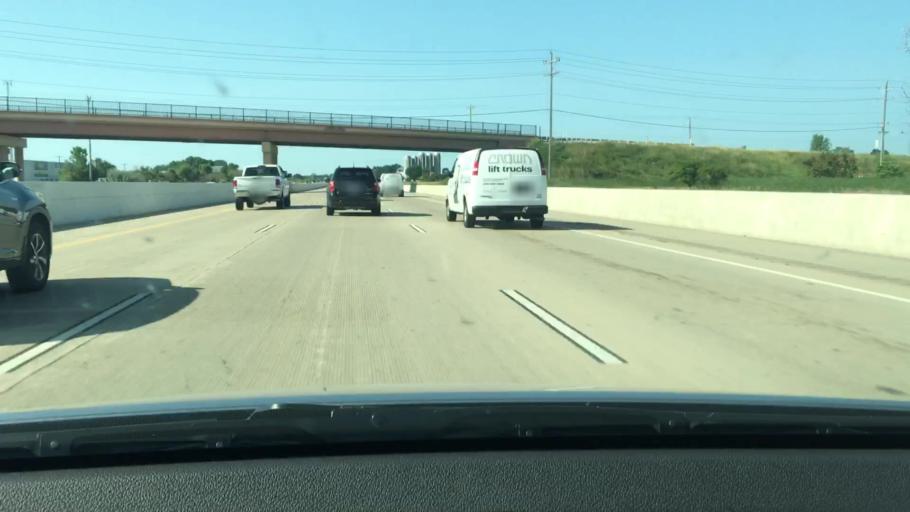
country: US
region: Wisconsin
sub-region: Winnebago County
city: Neenah
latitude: 44.1430
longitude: -88.4905
